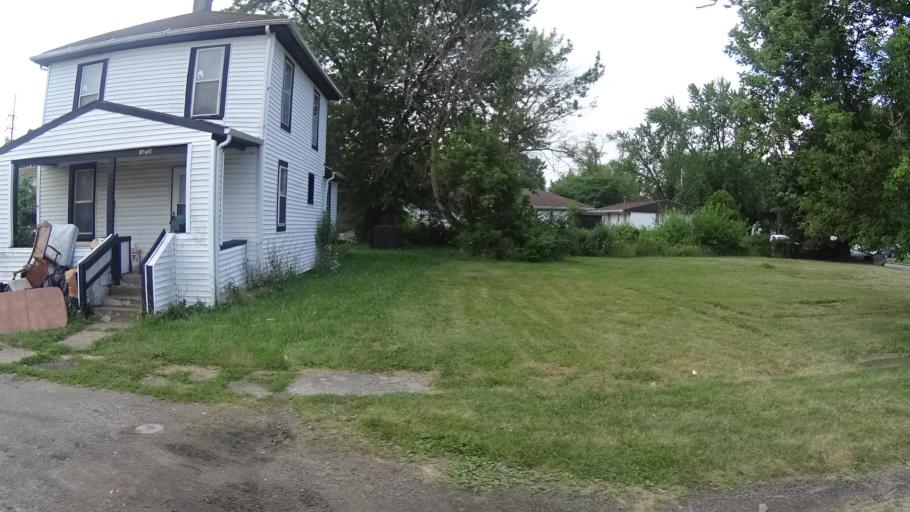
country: US
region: Ohio
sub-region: Erie County
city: Sandusky
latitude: 41.4387
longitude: -82.7208
